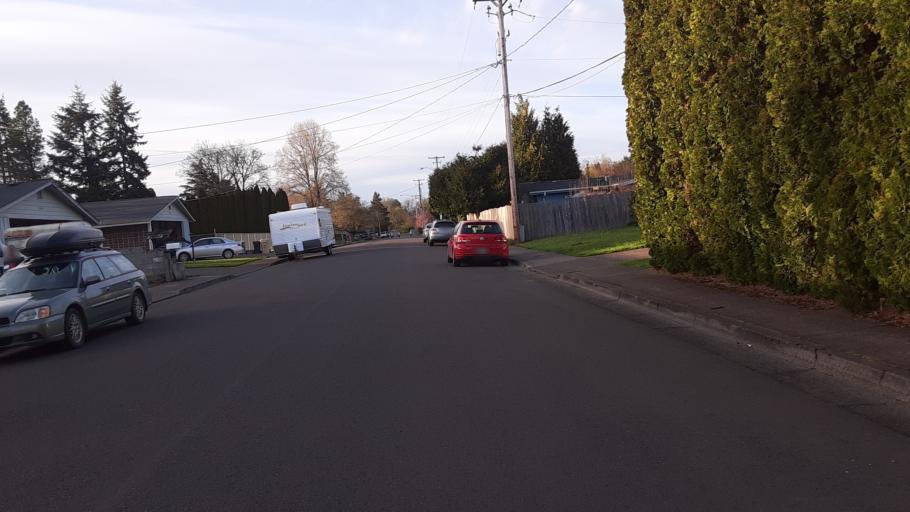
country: US
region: Oregon
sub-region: Benton County
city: Corvallis
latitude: 44.5417
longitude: -123.2586
